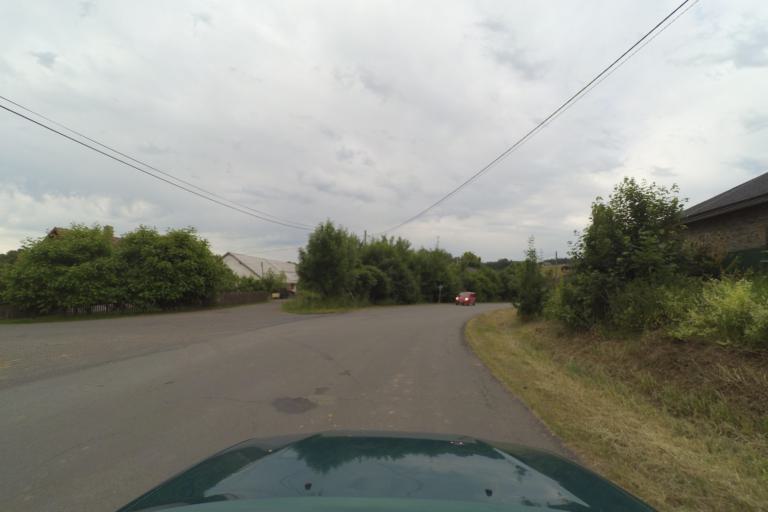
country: CZ
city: Cesky Dub
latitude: 50.6797
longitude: 14.9895
